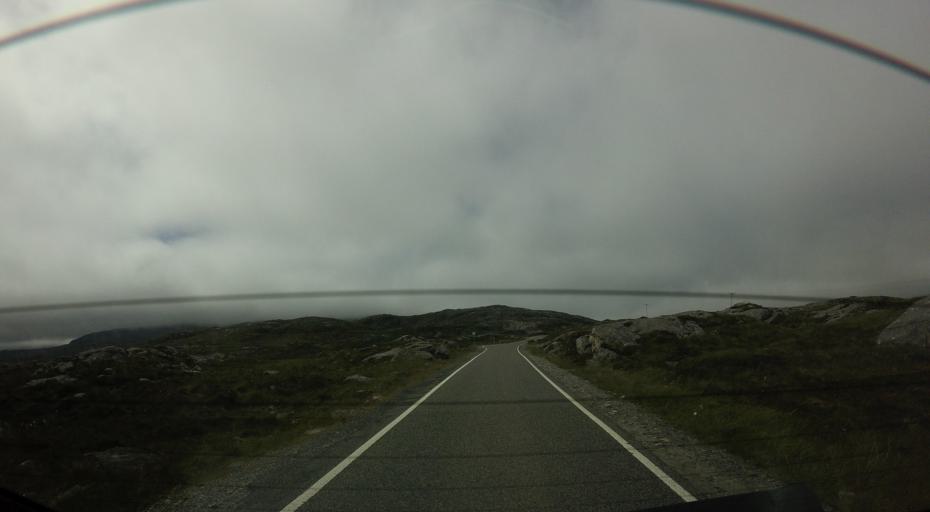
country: GB
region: Scotland
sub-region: Eilean Siar
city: Harris
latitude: 57.8491
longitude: -6.8412
